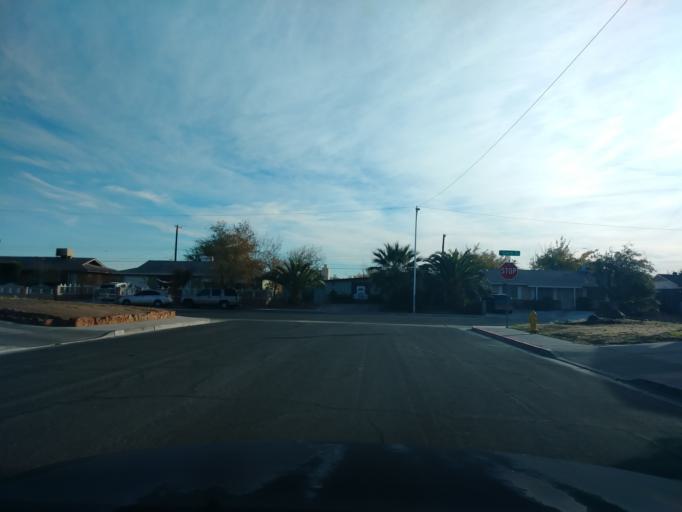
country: US
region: Nevada
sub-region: Clark County
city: Spring Valley
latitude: 36.1615
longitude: -115.2286
